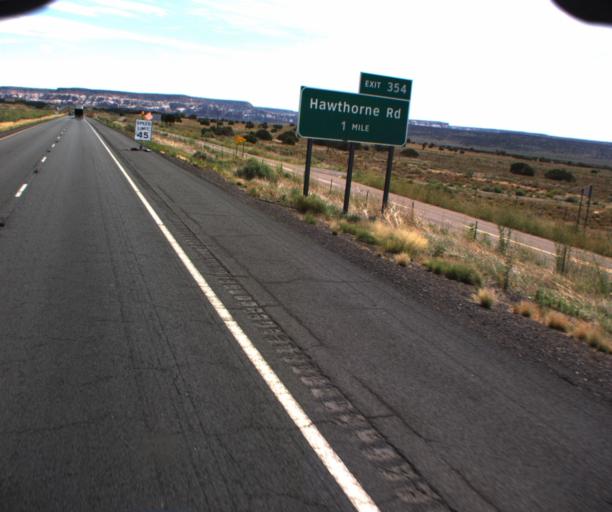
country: US
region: Arizona
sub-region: Apache County
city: Houck
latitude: 35.3025
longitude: -109.1249
